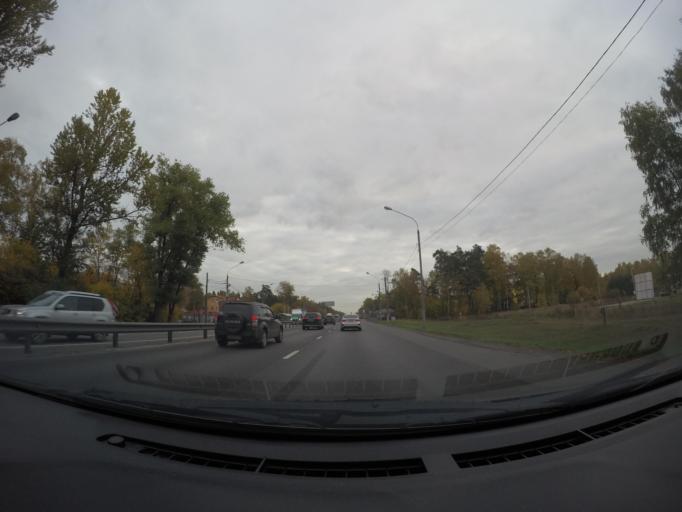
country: RU
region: Moskovskaya
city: Zarya
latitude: 55.8105
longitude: 38.0869
